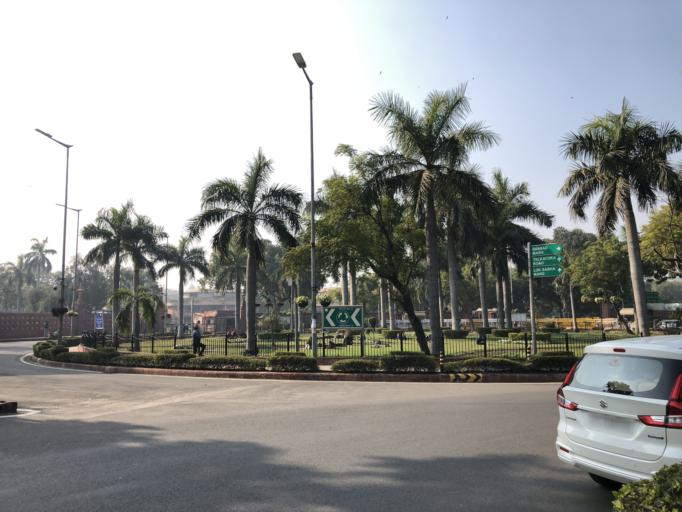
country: IN
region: NCT
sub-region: New Delhi
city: New Delhi
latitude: 28.6186
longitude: 77.2098
